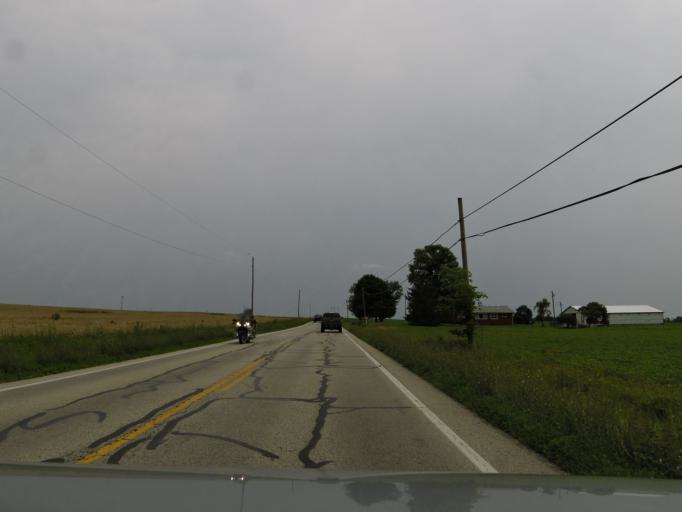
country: US
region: Ohio
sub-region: Warren County
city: Waynesville
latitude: 39.4904
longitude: -83.9602
